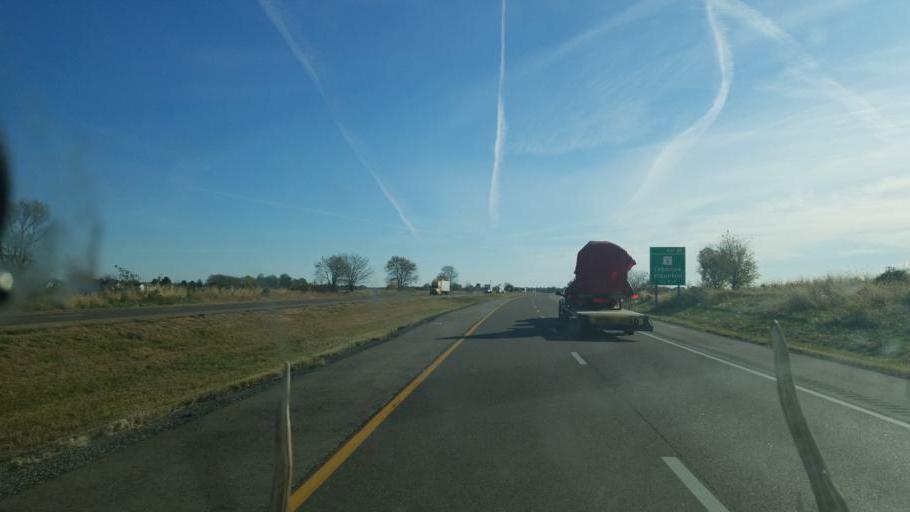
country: US
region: Illinois
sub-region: Madison County
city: Saint Jacob
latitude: 38.7624
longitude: -89.8173
